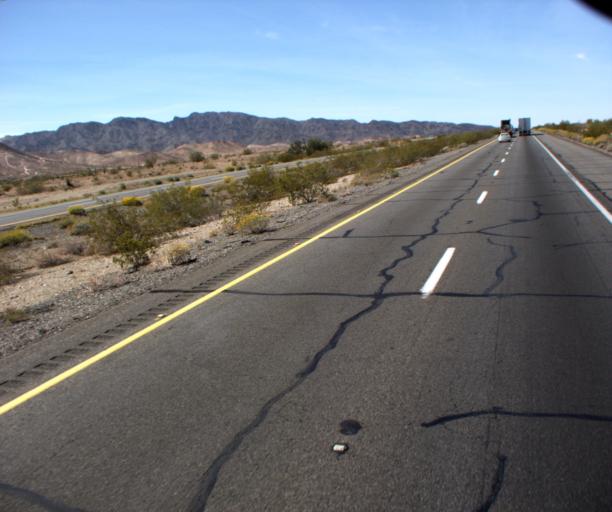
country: US
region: Arizona
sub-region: La Paz County
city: Quartzsite
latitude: 33.6510
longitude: -114.3031
